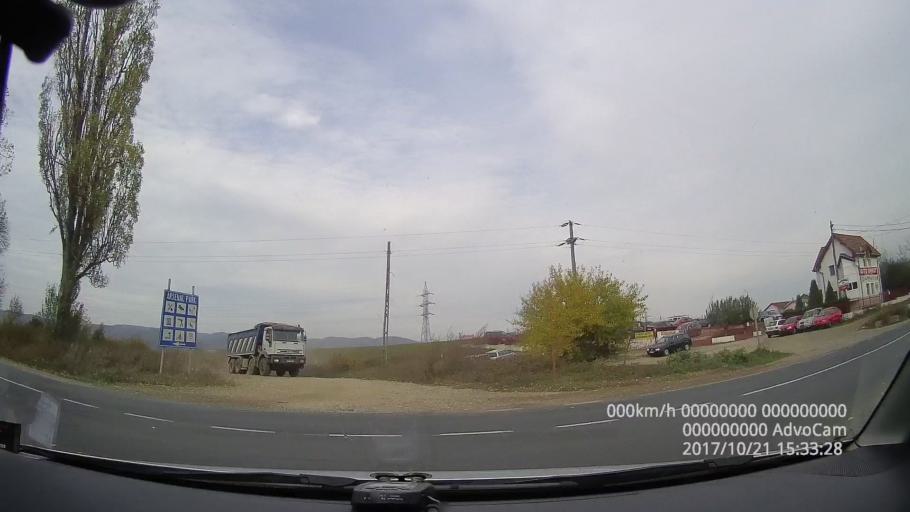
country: RO
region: Hunedoara
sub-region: Comuna Soimus
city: Soimus
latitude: 45.9054
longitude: 22.8781
